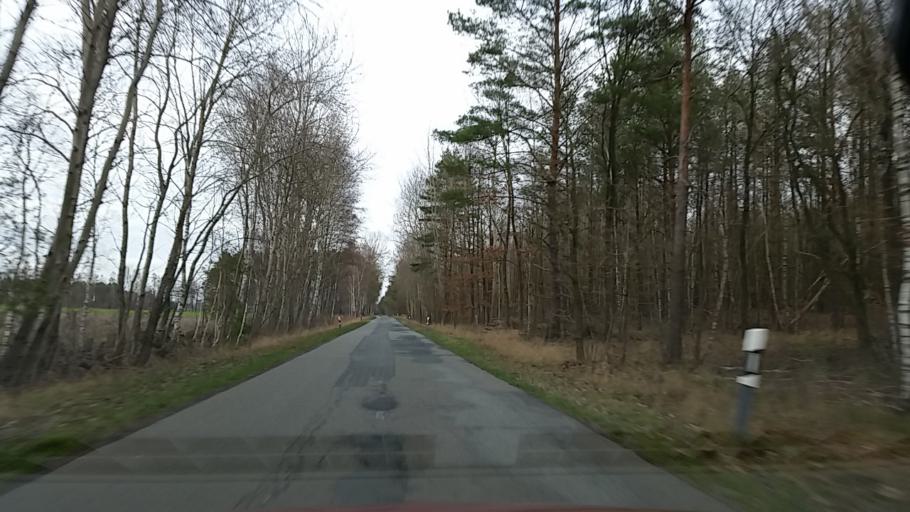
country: DE
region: Lower Saxony
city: Luder
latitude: 52.7862
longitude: 10.6691
